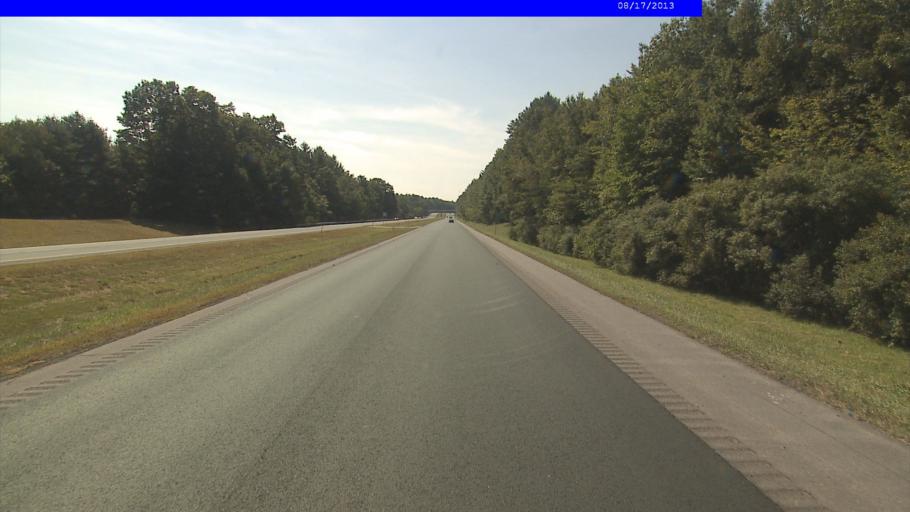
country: US
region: New Hampshire
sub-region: Cheshire County
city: Westmoreland
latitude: 43.0139
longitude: -72.4723
